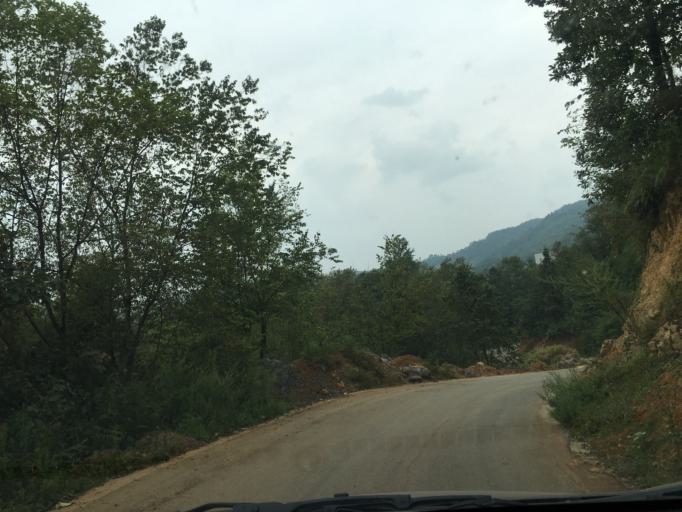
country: CN
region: Guangxi Zhuangzu Zizhiqu
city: Xinzhou
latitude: 25.5418
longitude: 105.5863
